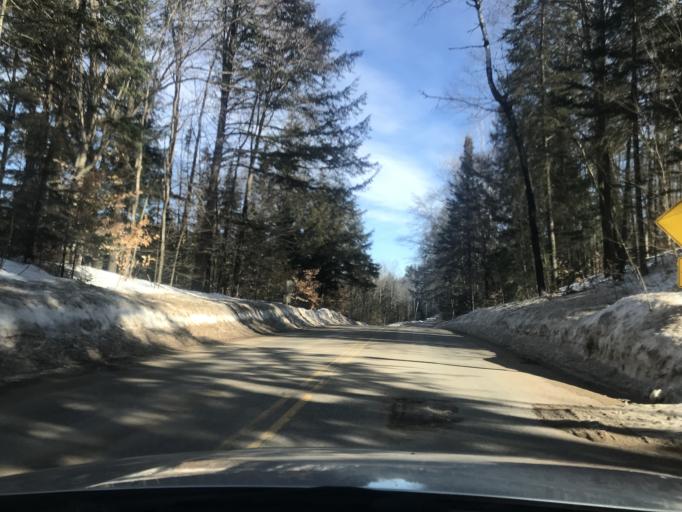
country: US
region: Michigan
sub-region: Dickinson County
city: Kingsford
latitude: 45.4065
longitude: -88.3694
